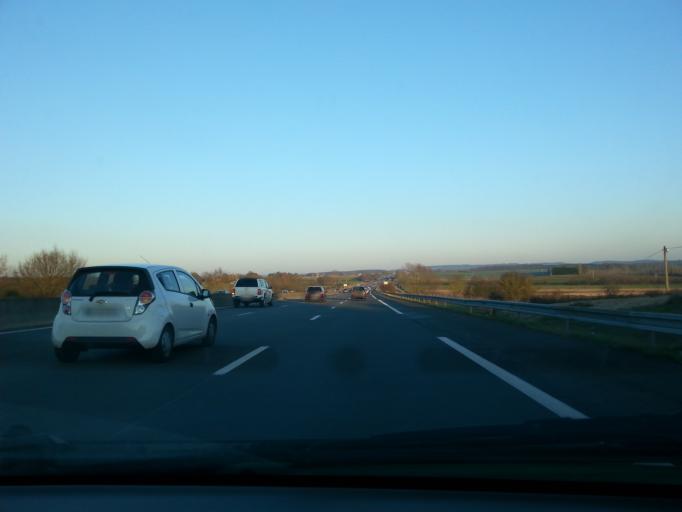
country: FR
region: Pays de la Loire
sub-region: Departement de la Sarthe
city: Cherre
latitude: 48.1366
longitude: 0.6453
